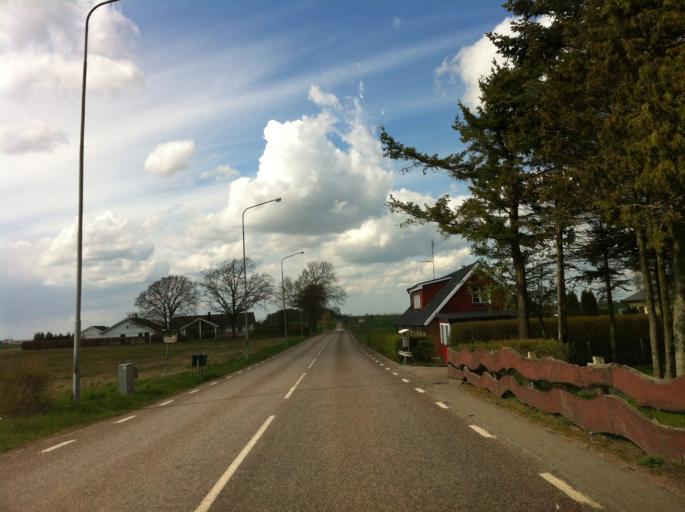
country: SE
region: Skane
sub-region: Eslovs Kommun
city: Eslov
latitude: 55.8286
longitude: 13.2694
